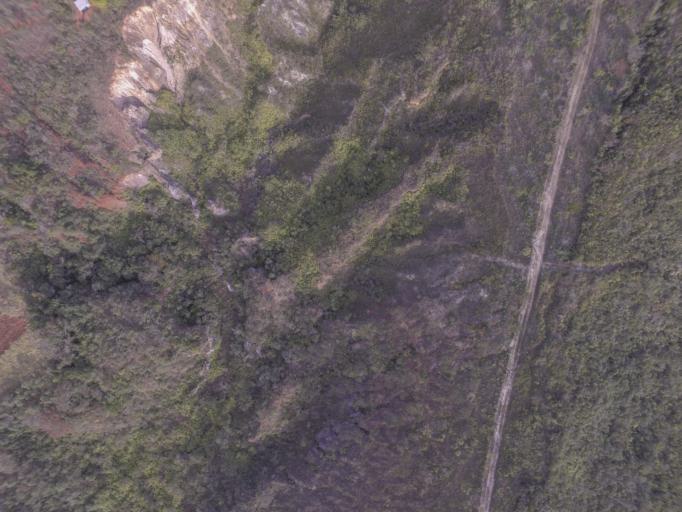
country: BR
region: Minas Gerais
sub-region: Tiradentes
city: Tiradentes
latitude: -21.0577
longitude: -44.1027
